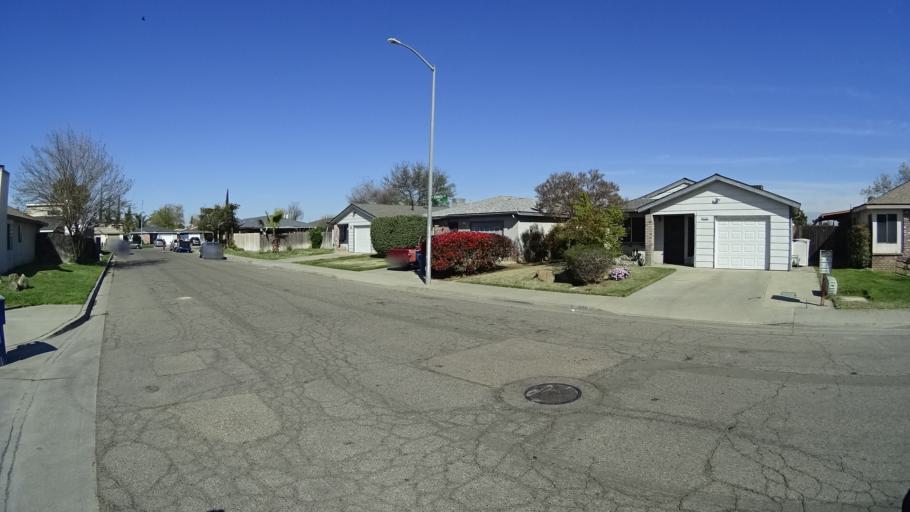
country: US
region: California
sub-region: Fresno County
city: West Park
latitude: 36.7995
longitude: -119.8823
